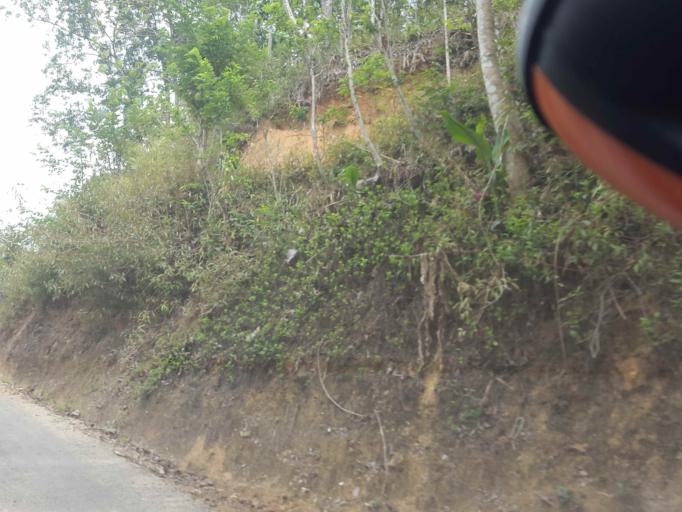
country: ID
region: East Java
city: Ploso
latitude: -8.0540
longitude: 111.1361
